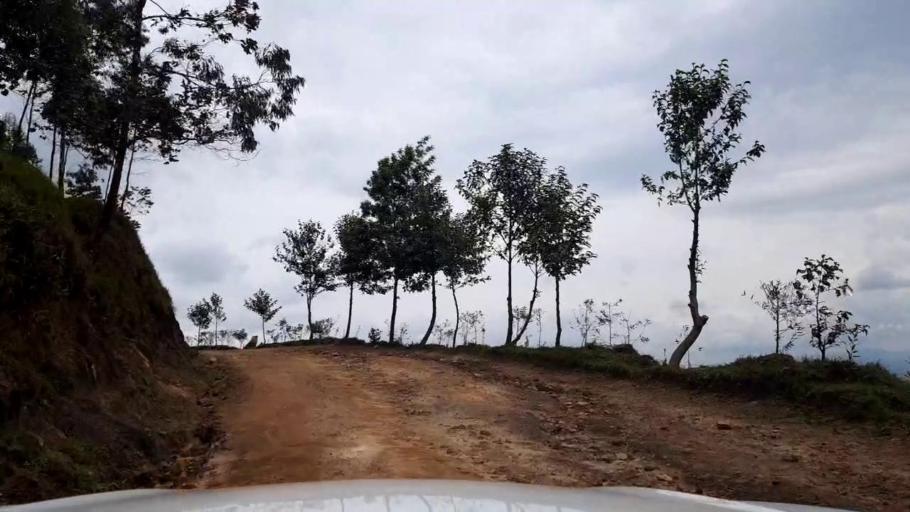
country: RW
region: Western Province
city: Kibuye
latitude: -1.9594
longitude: 29.4029
